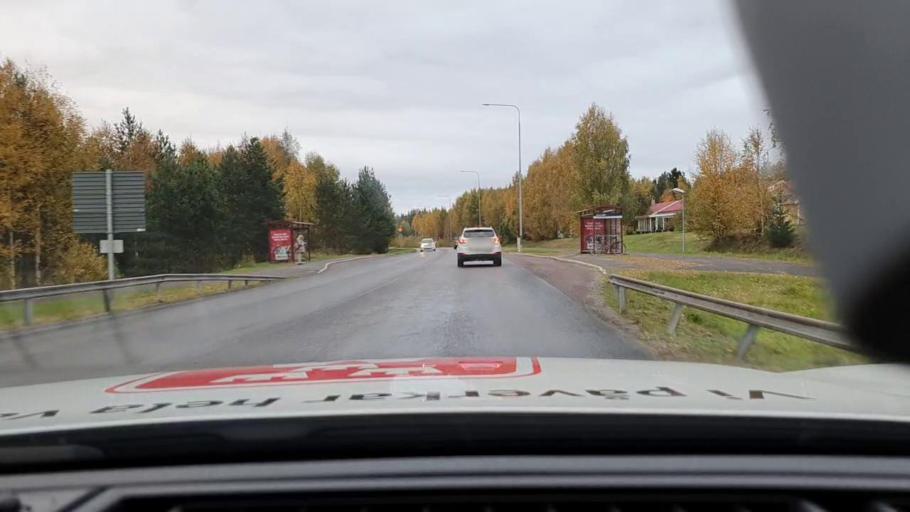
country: SE
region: Norrbotten
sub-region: Bodens Kommun
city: Saevast
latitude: 65.7620
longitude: 21.7387
